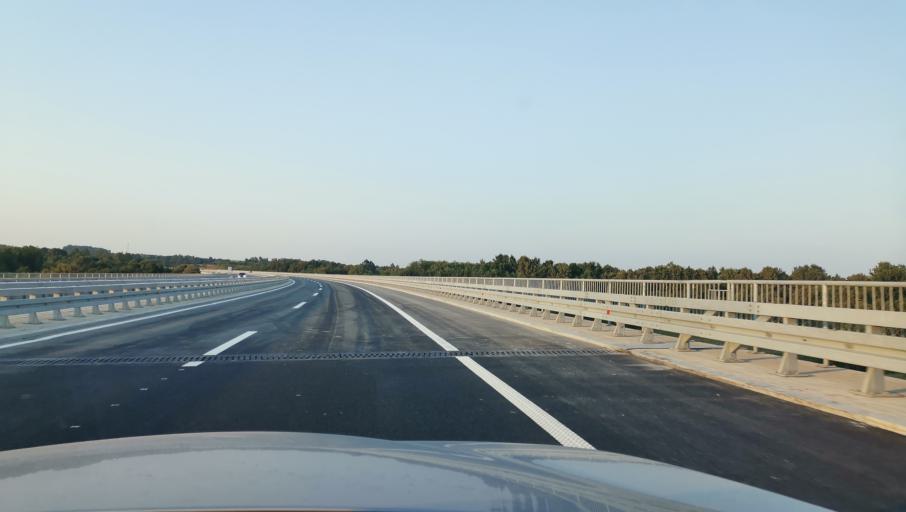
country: RS
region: Central Serbia
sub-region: Kolubarski Okrug
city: Ub
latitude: 44.4152
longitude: 20.1027
